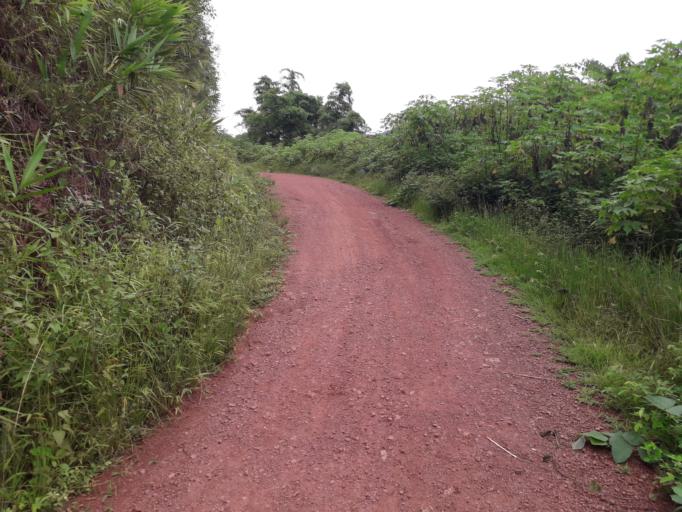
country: CN
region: Yunnan
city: Menglie
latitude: 22.2423
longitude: 101.6108
